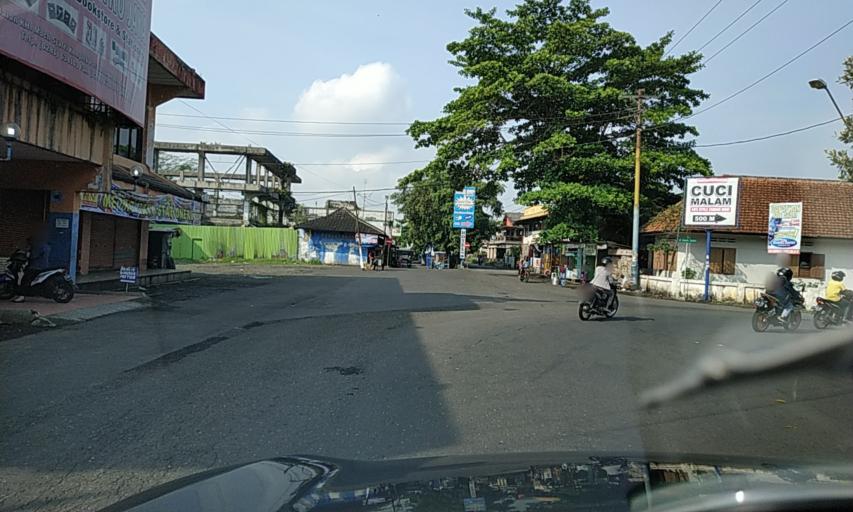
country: ID
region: Central Java
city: Purwokerto
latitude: -7.4235
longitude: 109.2424
